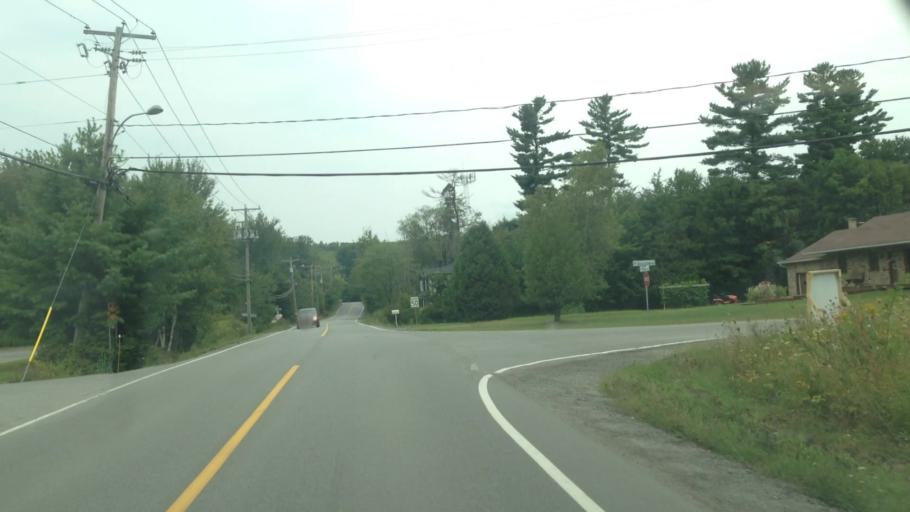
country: CA
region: Quebec
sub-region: Laurentides
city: Saint-Jerome
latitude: 45.8232
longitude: -73.9756
